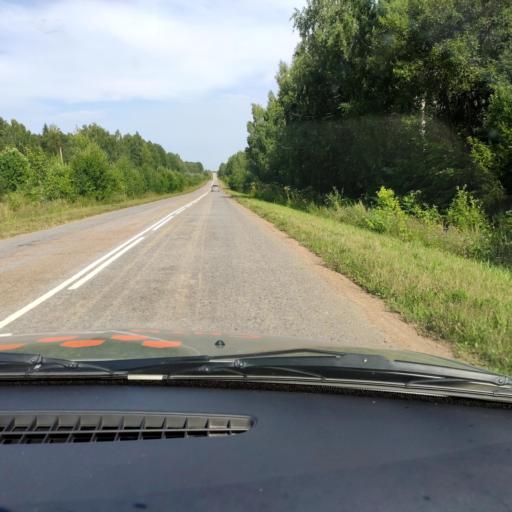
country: RU
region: Bashkortostan
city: Pavlovka
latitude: 55.3915
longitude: 56.5312
